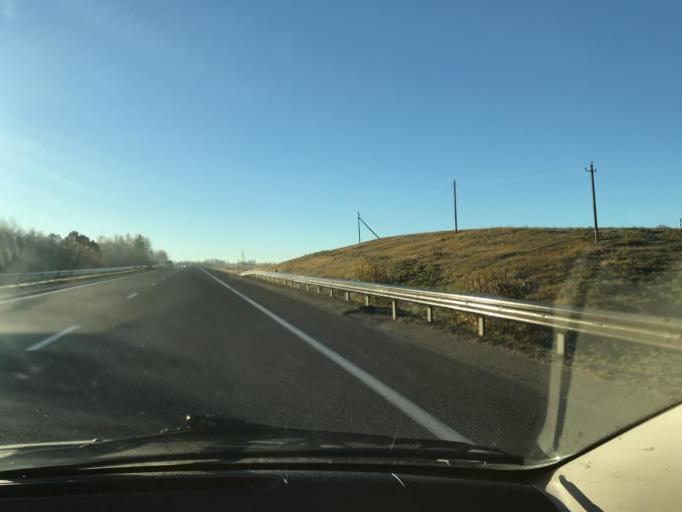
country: BY
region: Vitebsk
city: Vitebsk
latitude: 55.0941
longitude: 30.3031
